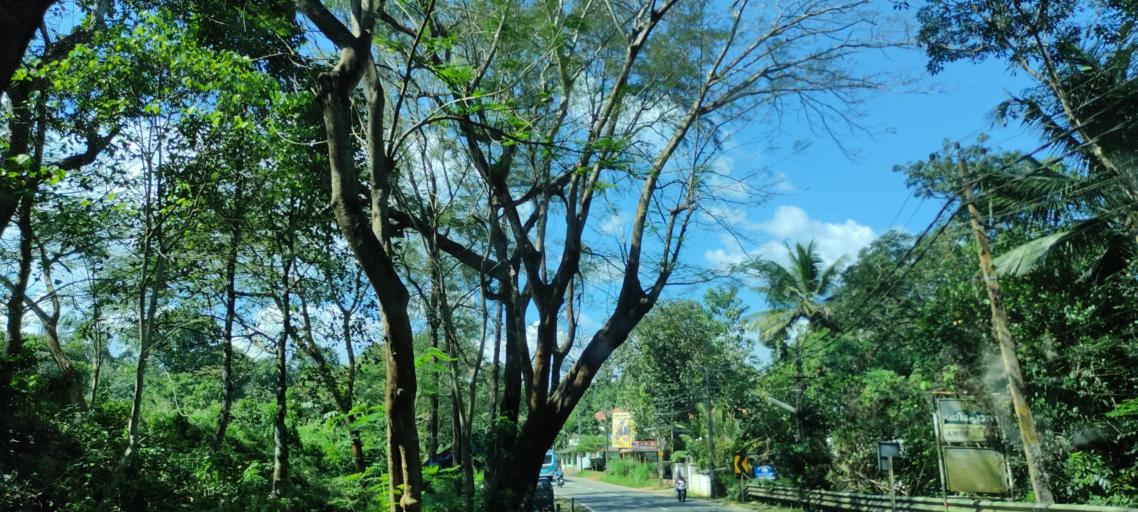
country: IN
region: Kerala
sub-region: Pattanamtitta
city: Adur
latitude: 9.1628
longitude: 76.7440
